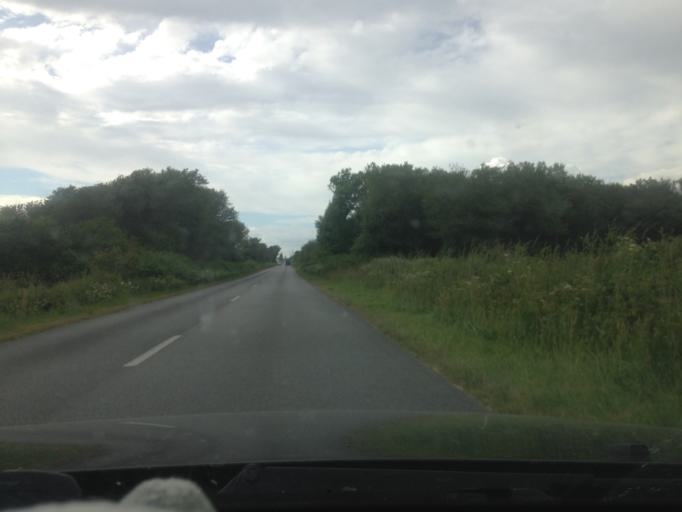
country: FR
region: Brittany
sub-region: Departement du Morbihan
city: Erdeven
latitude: 47.6233
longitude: -3.1379
